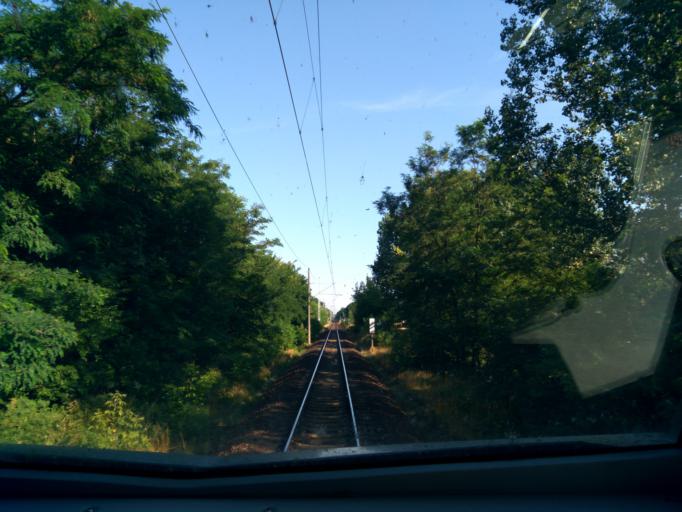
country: DE
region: Brandenburg
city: Vetschau
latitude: 51.8133
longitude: 14.0356
